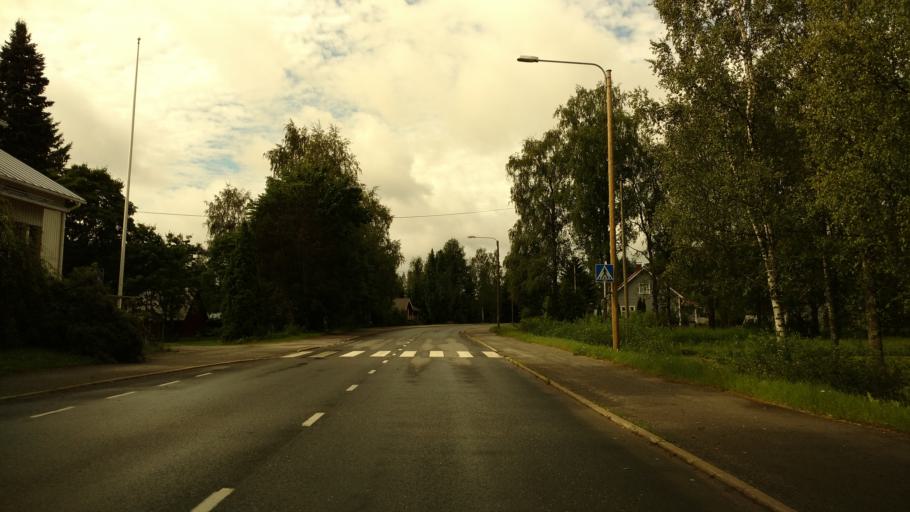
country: FI
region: Varsinais-Suomi
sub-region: Loimaa
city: Koski Tl
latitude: 60.6588
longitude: 23.1464
